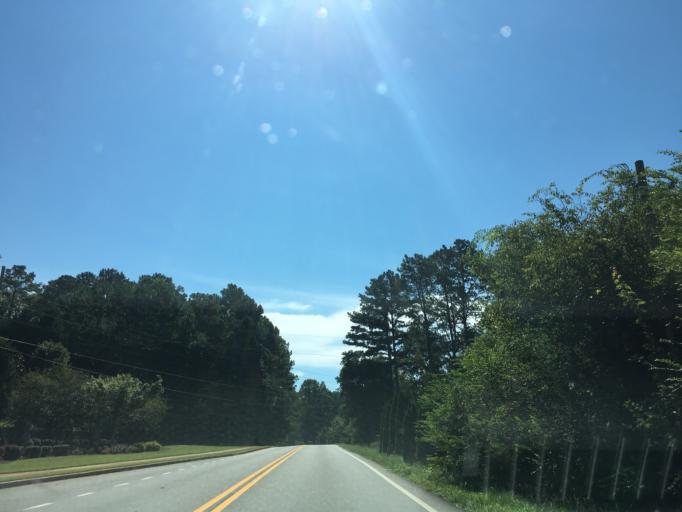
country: US
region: Georgia
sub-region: Fulton County
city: Milton
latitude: 34.1634
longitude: -84.3129
